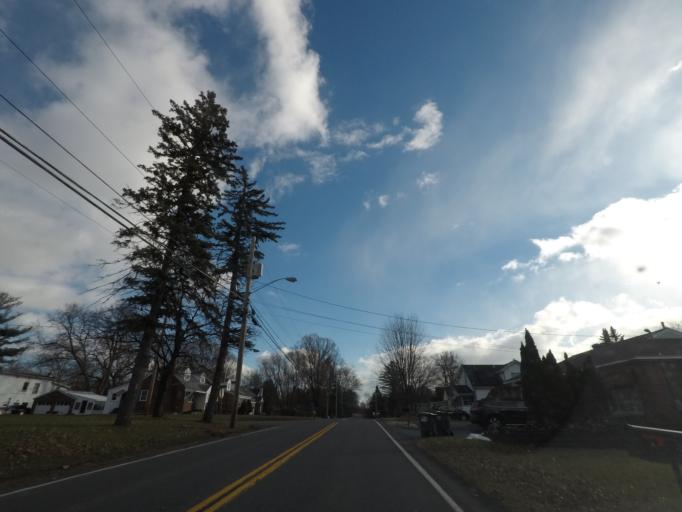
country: US
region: New York
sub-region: Schenectady County
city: Niskayuna
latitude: 42.7629
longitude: -73.8891
